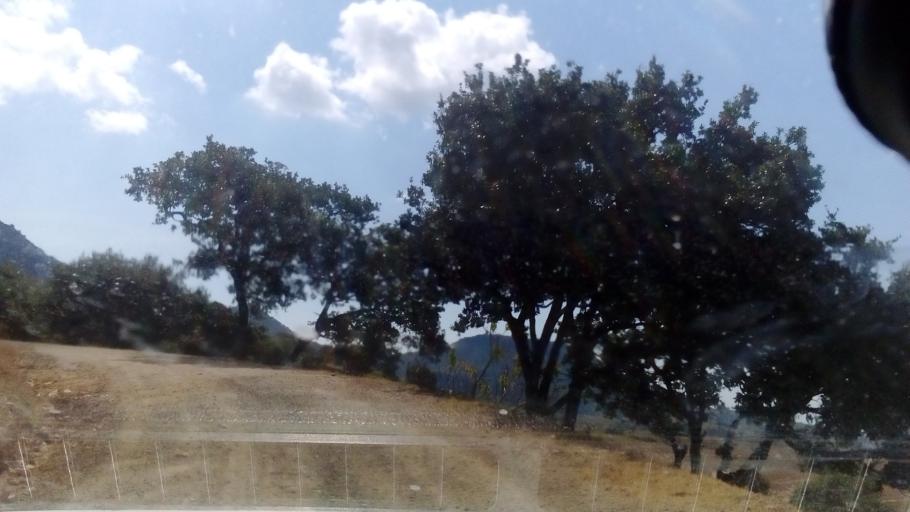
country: MX
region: Guanajuato
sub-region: Silao de la Victoria
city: San Francisco (Banos de Agua Caliente)
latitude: 21.1660
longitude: -101.4623
